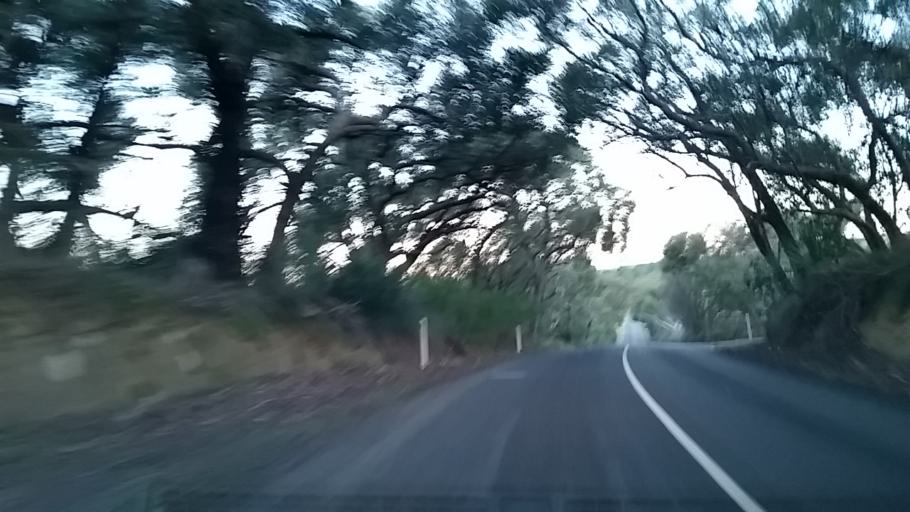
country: AU
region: South Australia
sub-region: Alexandrina
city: Mount Compass
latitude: -35.3105
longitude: 138.6177
